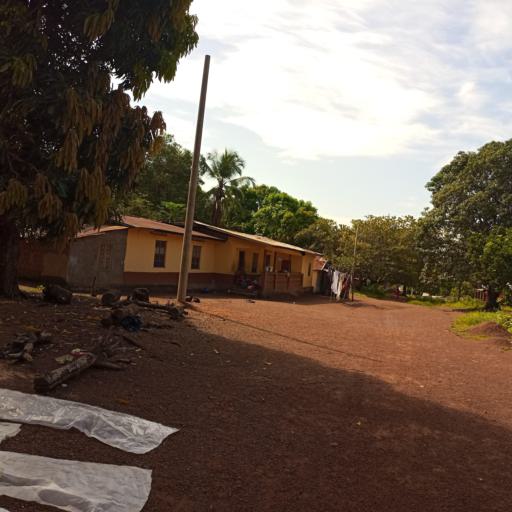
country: SL
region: Northern Province
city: Kambia
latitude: 9.1205
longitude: -12.9146
